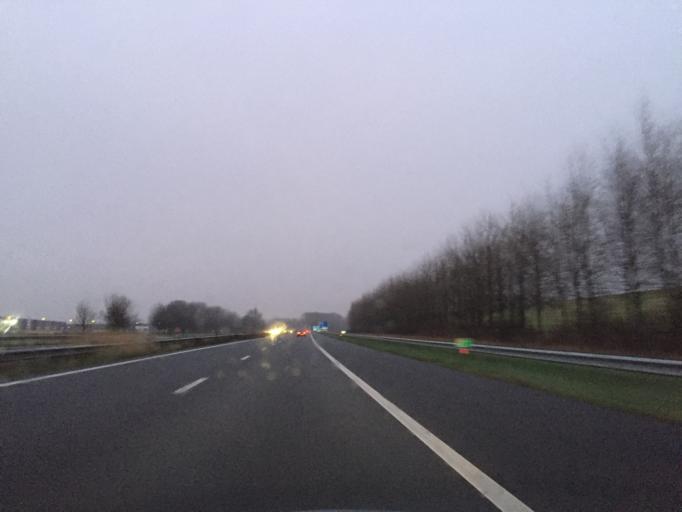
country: NL
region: North Brabant
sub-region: Gemeente Moerdijk
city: Klundert
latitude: 51.6667
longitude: 4.5942
